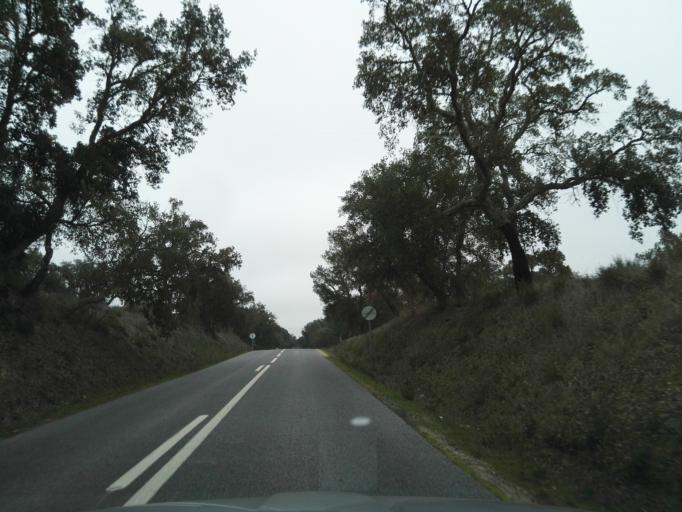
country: PT
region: Evora
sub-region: Vendas Novas
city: Vendas Novas
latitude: 38.7664
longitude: -8.3885
